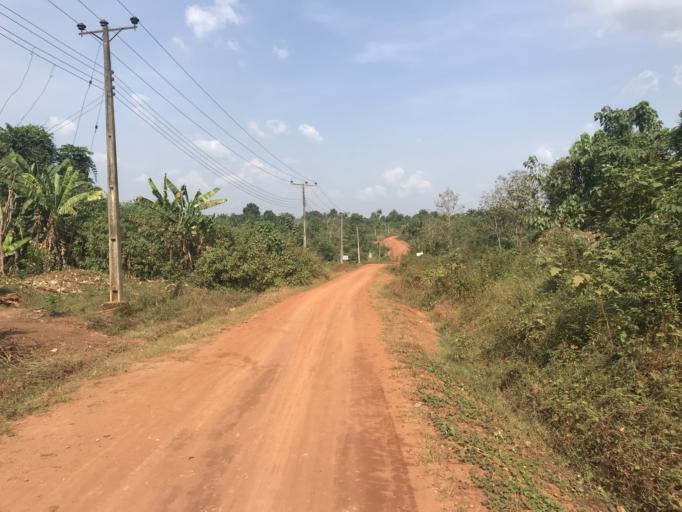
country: NG
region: Osun
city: Ilesa
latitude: 7.6530
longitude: 4.6659
